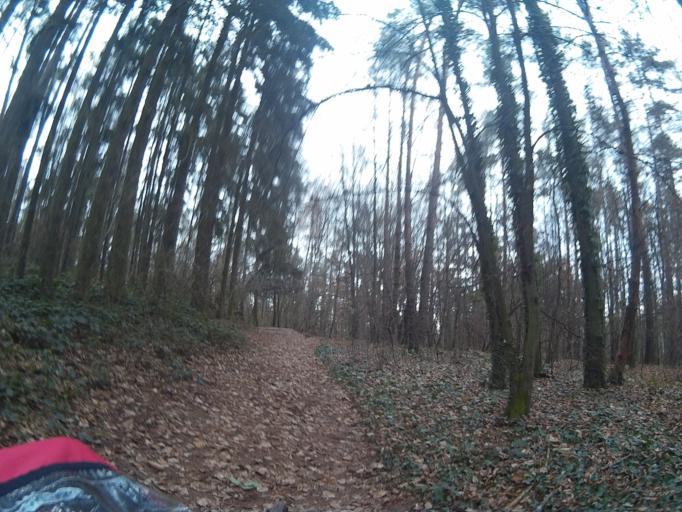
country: CZ
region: Plzensky
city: Stary Plzenec
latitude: 49.6806
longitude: 13.4813
